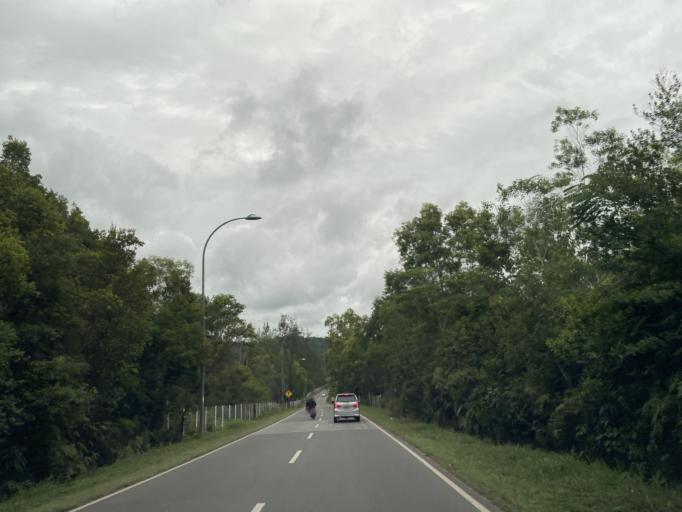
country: SG
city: Singapore
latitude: 1.1133
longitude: 104.0136
